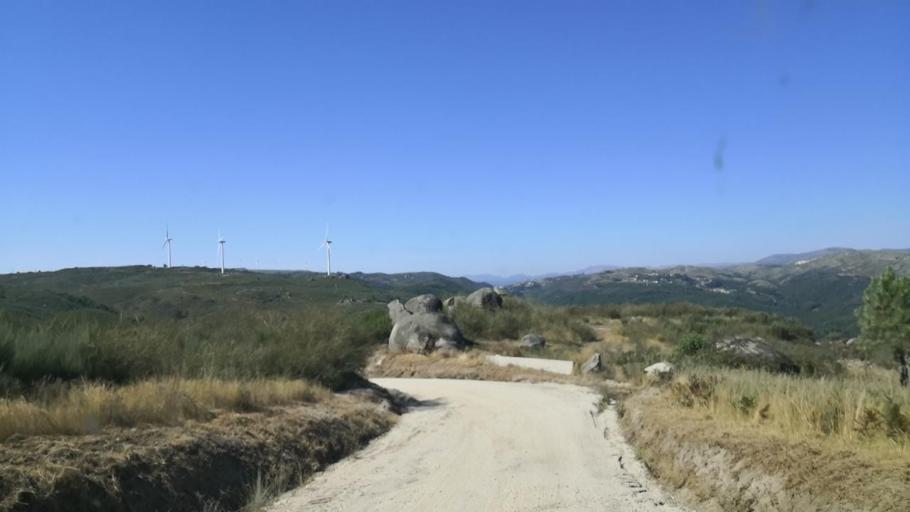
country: PT
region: Braga
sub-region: Cabeceiras de Basto
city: Refojos de Basto
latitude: 41.4963
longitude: -8.0719
